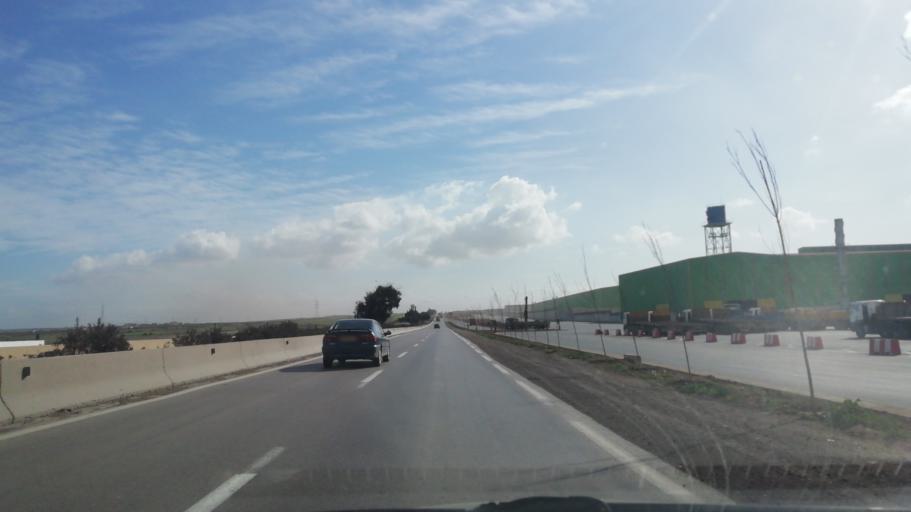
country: DZ
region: Oran
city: Ain el Bya
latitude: 35.7765
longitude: -0.2587
